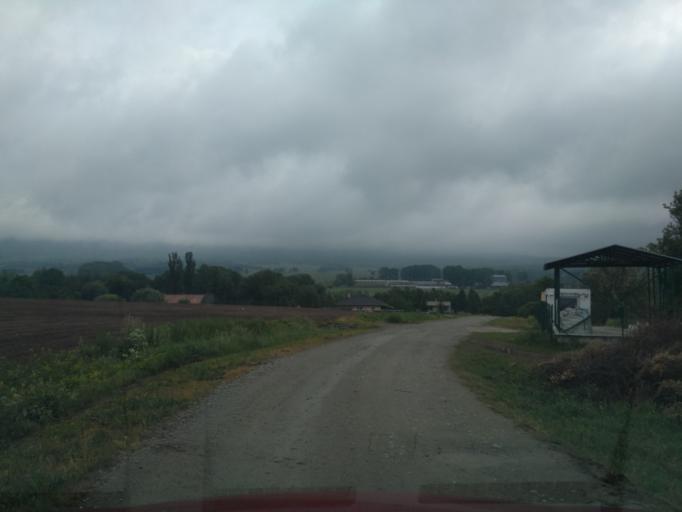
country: SK
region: Kosicky
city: Secovce
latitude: 48.7649
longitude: 21.4780
